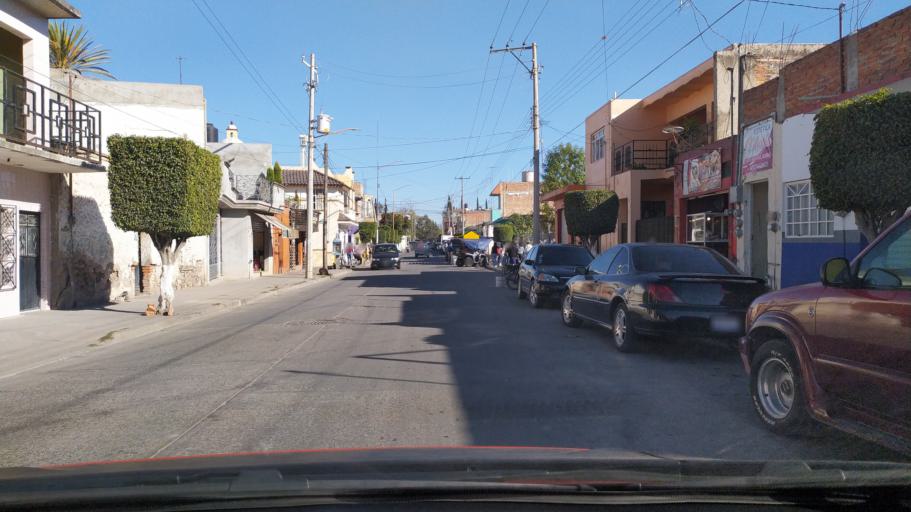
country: MX
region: Guanajuato
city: Ciudad Manuel Doblado
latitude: 20.7250
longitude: -101.9486
